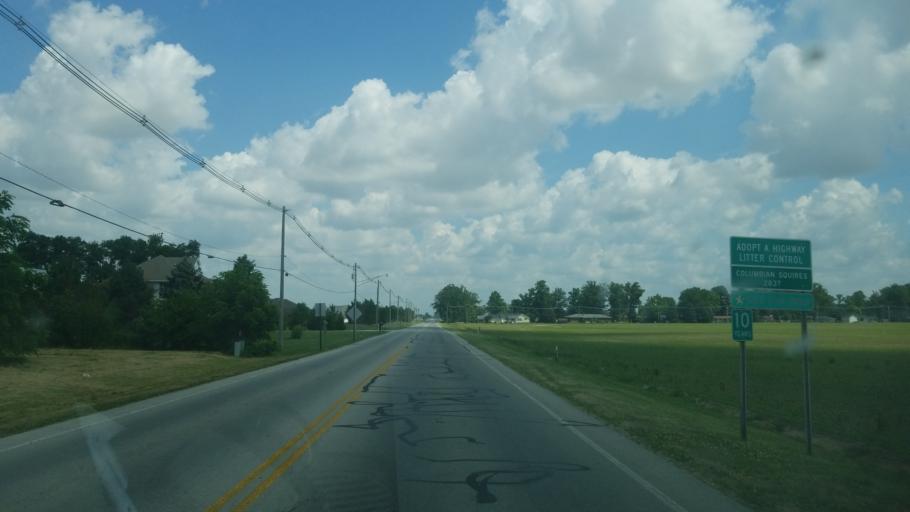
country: US
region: Ohio
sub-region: Auglaize County
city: Wapakoneta
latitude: 40.5860
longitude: -84.2028
